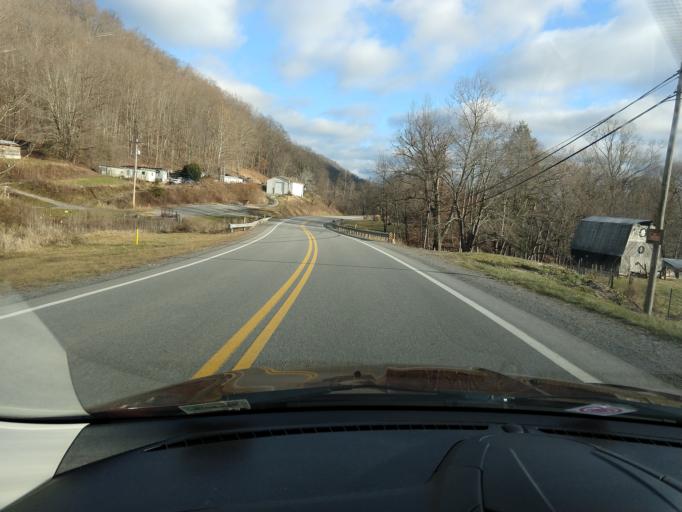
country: US
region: West Virginia
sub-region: Randolph County
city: Elkins
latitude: 38.7559
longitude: -79.9559
